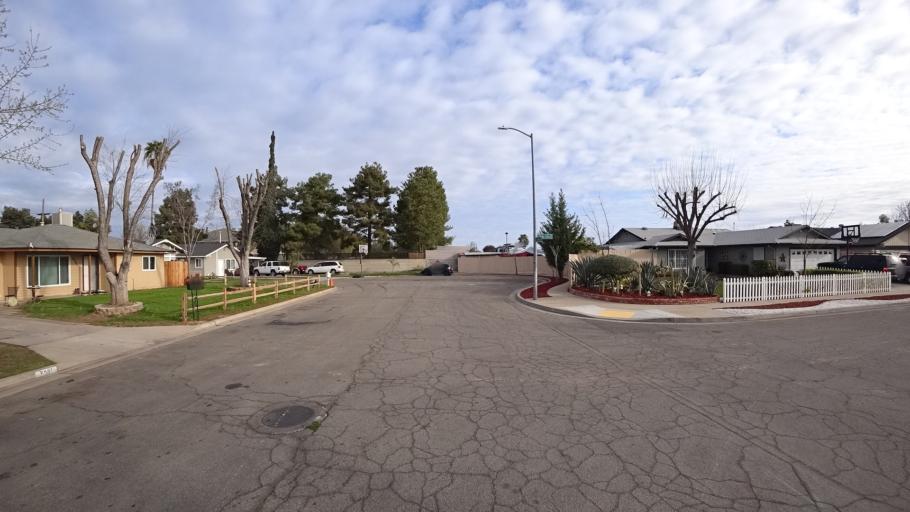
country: US
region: California
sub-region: Fresno County
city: Fresno
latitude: 36.8333
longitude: -119.7970
